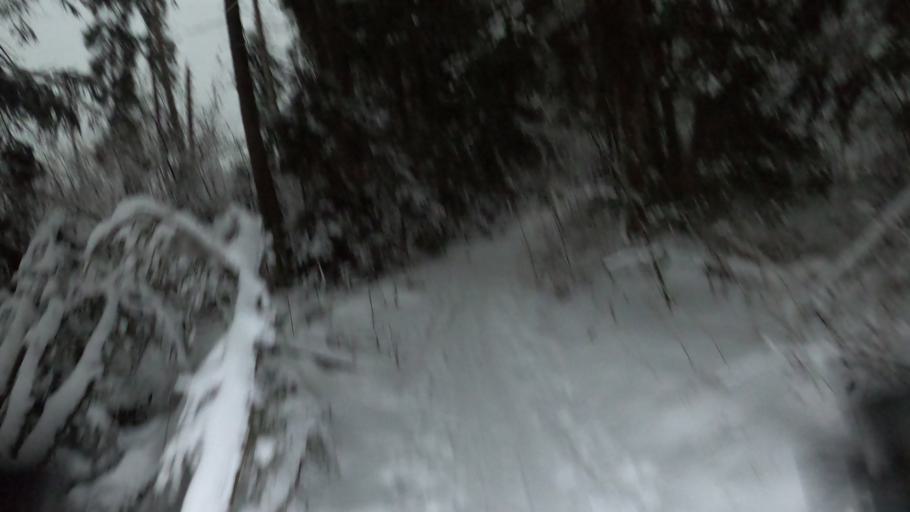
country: RU
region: Moskovskaya
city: Nakhabino
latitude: 55.8936
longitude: 37.2088
